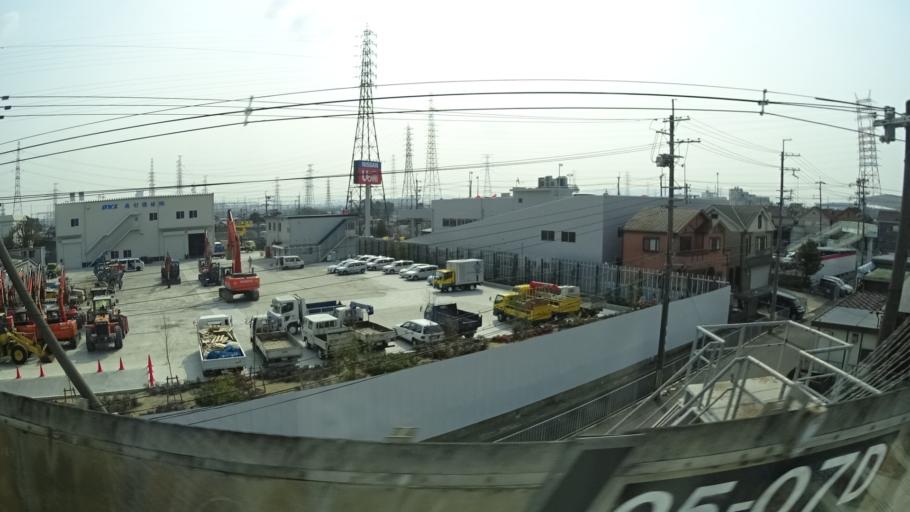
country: JP
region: Osaka
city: Takatsuki
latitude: 34.8613
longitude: 135.6508
